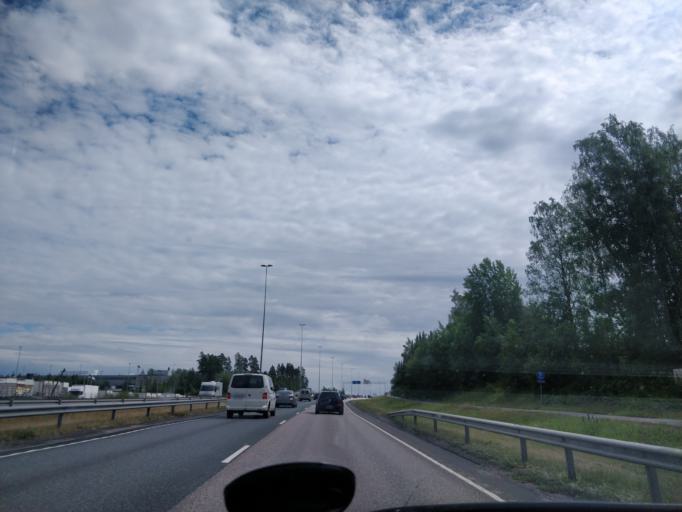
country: FI
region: Uusimaa
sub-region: Helsinki
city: Teekkarikylae
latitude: 60.2980
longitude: 24.9032
